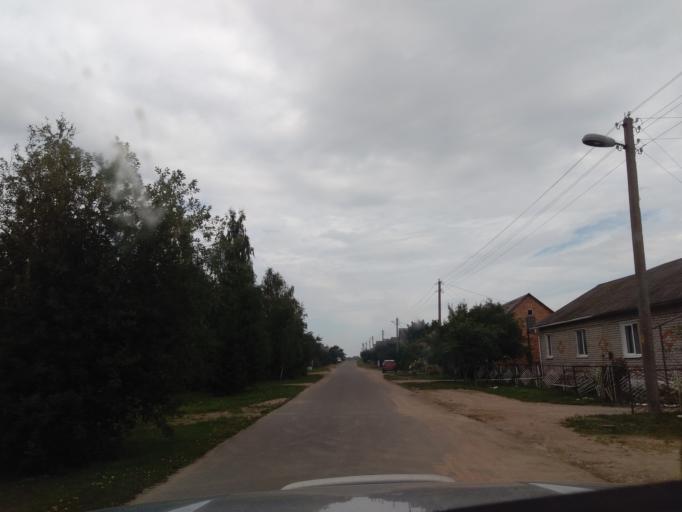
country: BY
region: Minsk
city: Kapyl'
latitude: 53.1557
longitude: 27.0698
